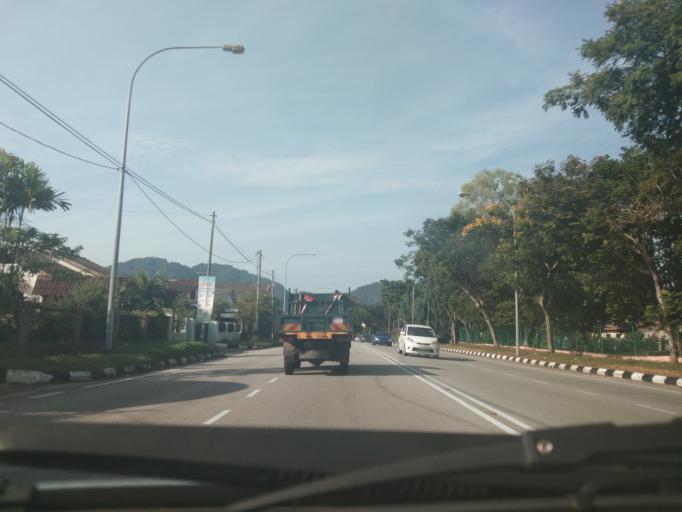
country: MY
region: Perak
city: Ipoh
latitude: 4.5759
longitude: 101.1273
